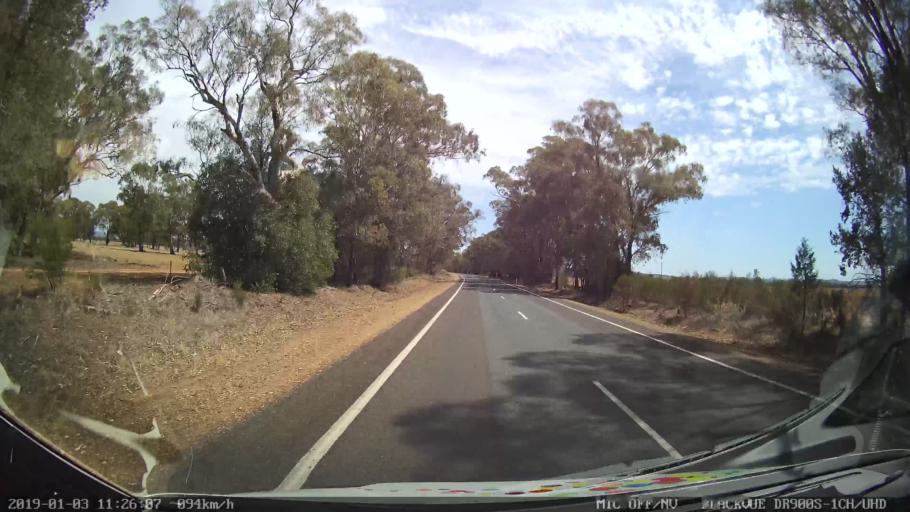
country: AU
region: New South Wales
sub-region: Weddin
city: Grenfell
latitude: -34.0294
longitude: 148.2269
